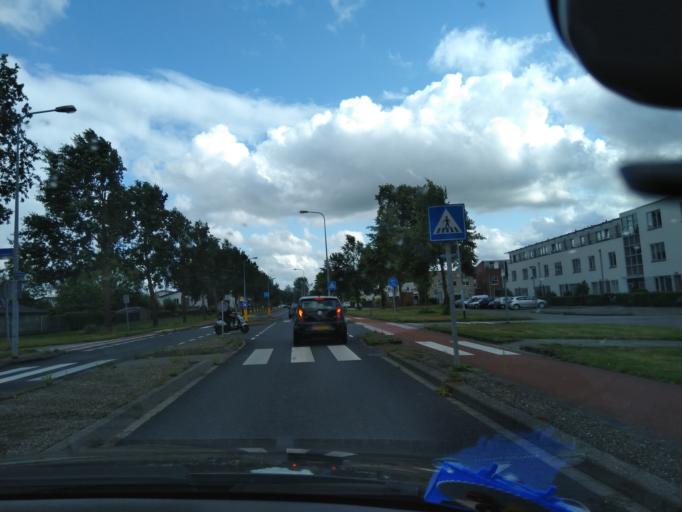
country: NL
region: Groningen
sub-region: Gemeente Groningen
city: Groningen
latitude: 53.2036
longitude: 6.5098
